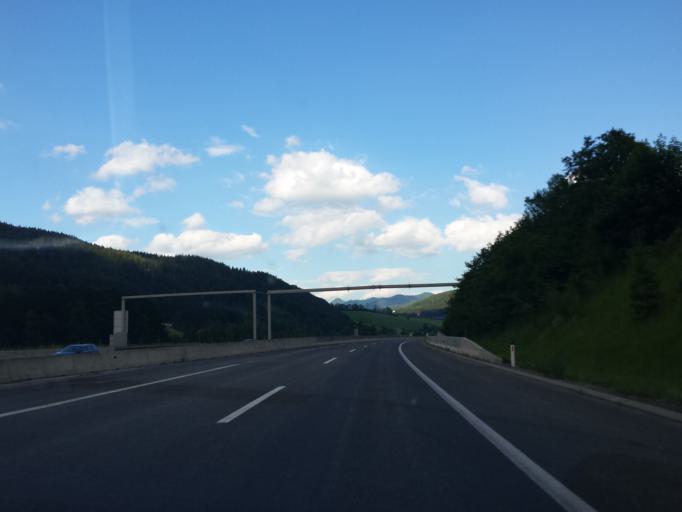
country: AT
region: Styria
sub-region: Politischer Bezirk Bruck-Muerzzuschlag
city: Muerzzuschlag
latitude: 47.6026
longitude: 15.6944
